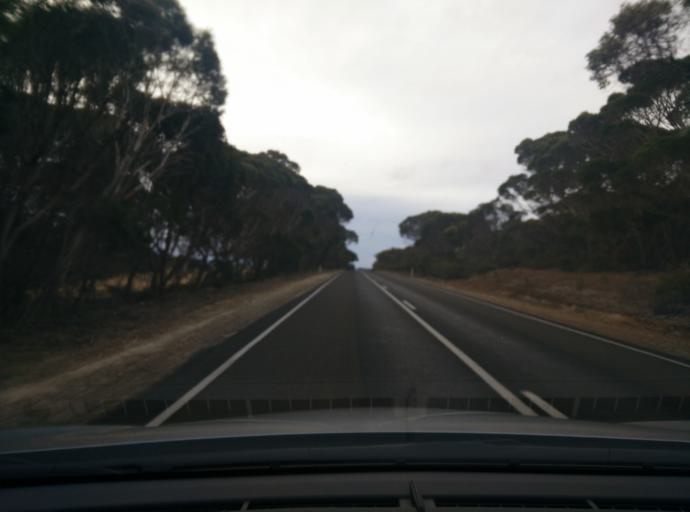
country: AU
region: South Australia
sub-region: Kangaroo Island
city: Kingscote
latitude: -35.8096
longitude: 137.6790
